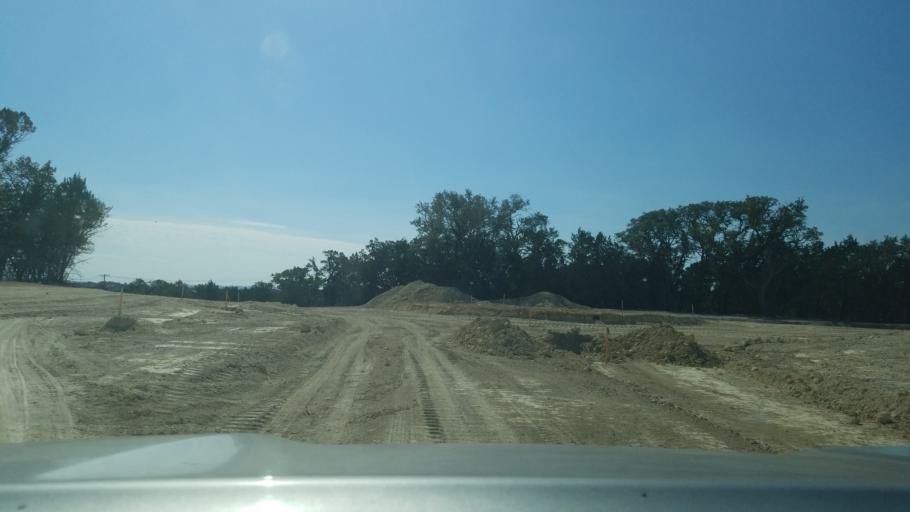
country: US
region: Texas
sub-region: Kendall County
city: Boerne
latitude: 29.7576
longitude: -98.7174
